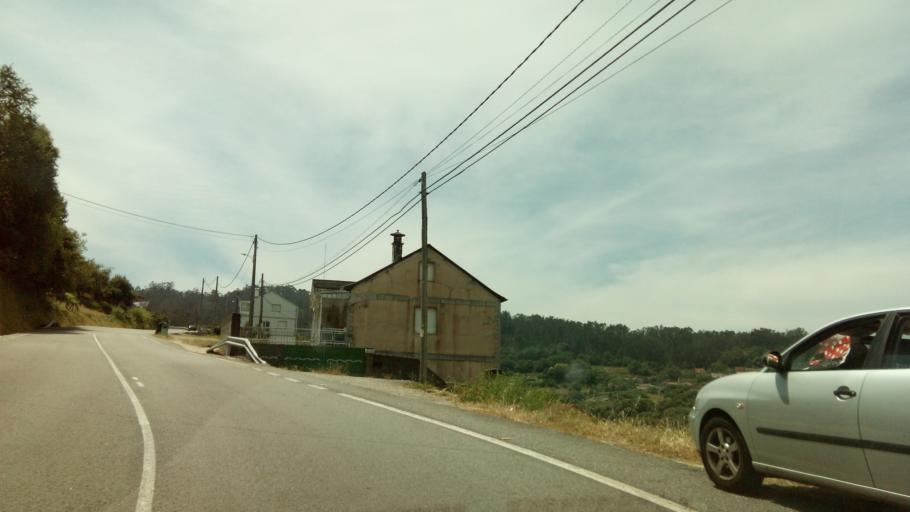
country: ES
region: Galicia
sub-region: Provincia de Pontevedra
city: Marin
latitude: 42.3493
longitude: -8.7016
